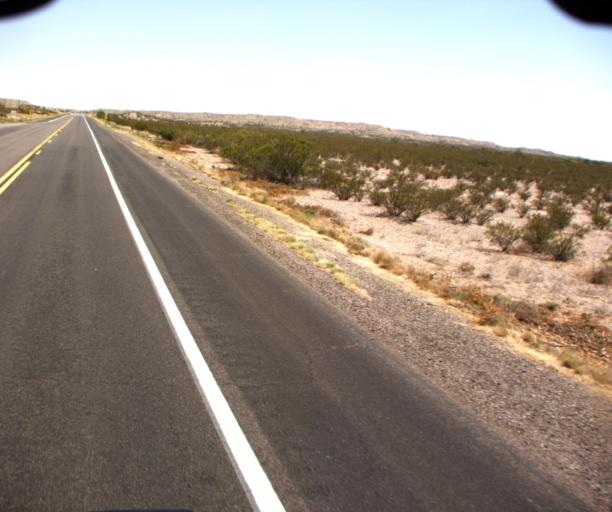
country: US
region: Arizona
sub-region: Greenlee County
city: Clifton
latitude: 32.6555
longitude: -109.0626
